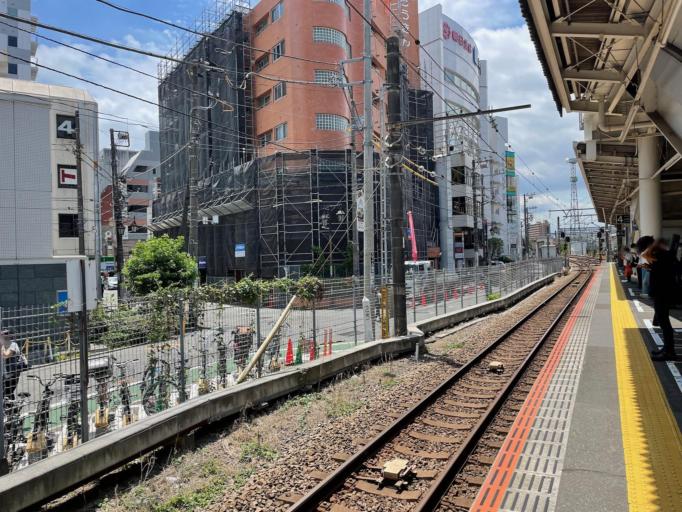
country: JP
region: Kanagawa
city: Fujisawa
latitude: 35.3385
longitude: 139.4865
